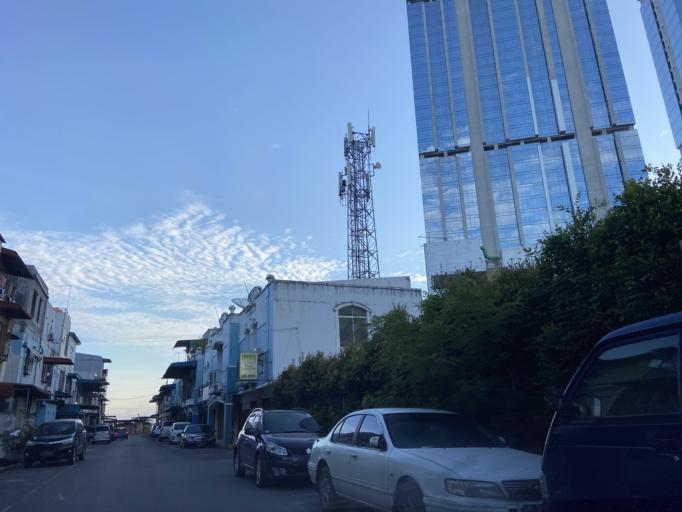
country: SG
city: Singapore
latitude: 1.1199
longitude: 104.0438
